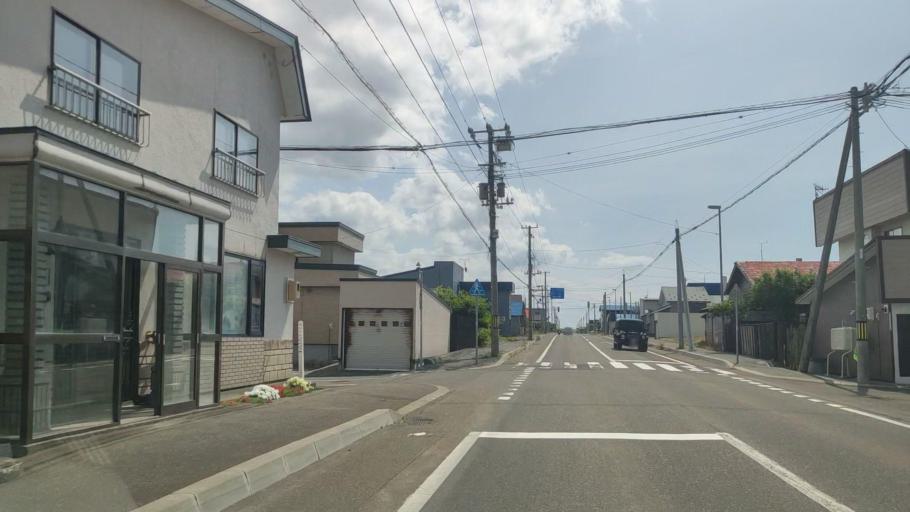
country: JP
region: Hokkaido
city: Makubetsu
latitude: 44.8840
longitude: 141.7427
